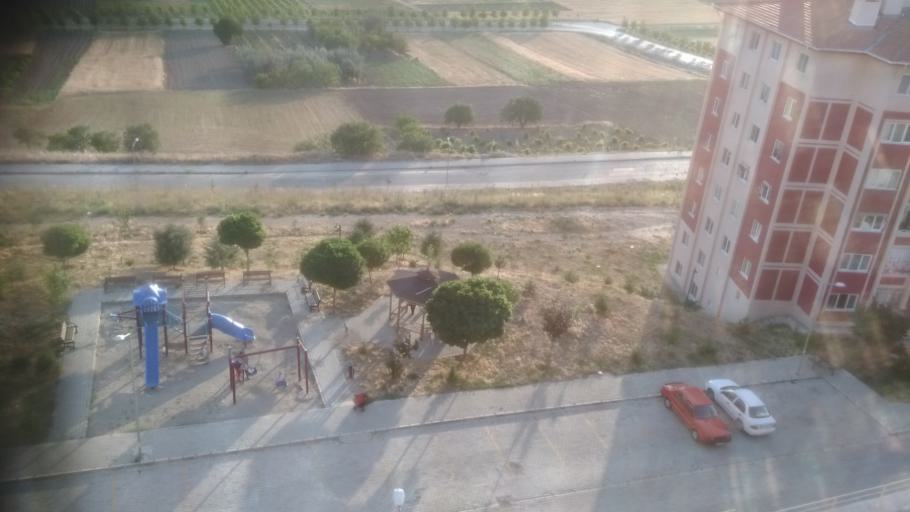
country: TR
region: Isparta
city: Isparta
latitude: 37.8237
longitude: 30.5775
